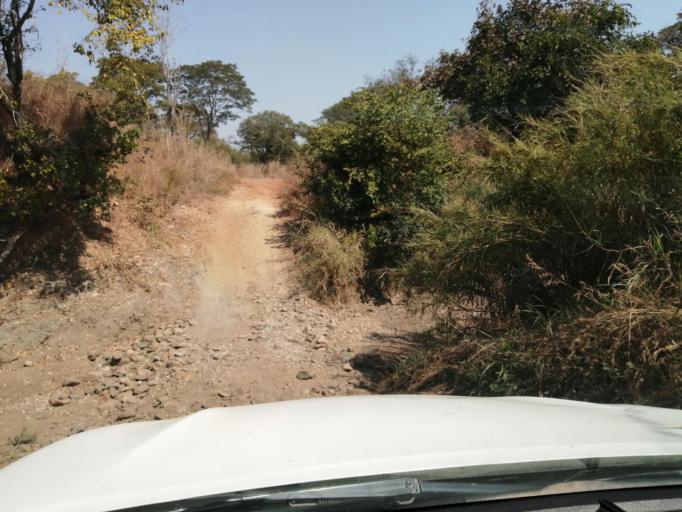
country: ZM
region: Eastern
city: Nyimba
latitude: -14.3474
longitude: 30.0210
